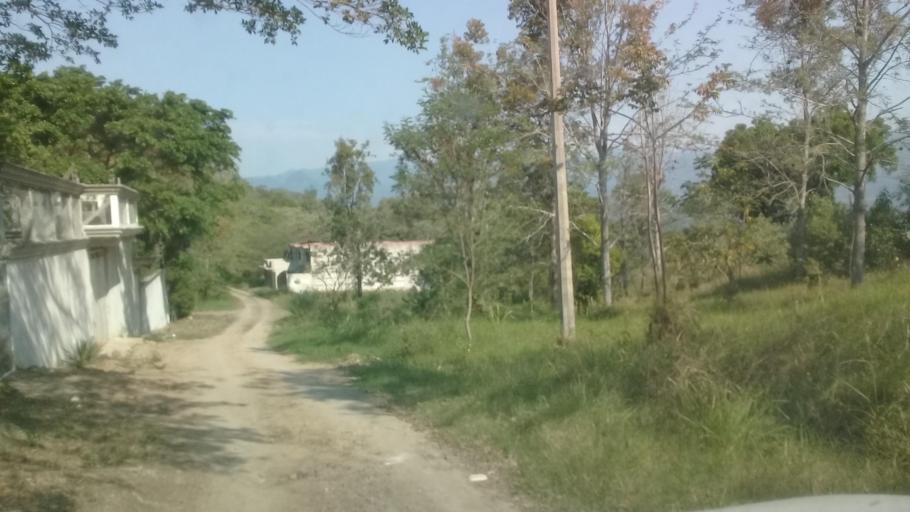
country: MX
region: Veracruz
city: El Castillo
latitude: 19.5723
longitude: -96.8364
